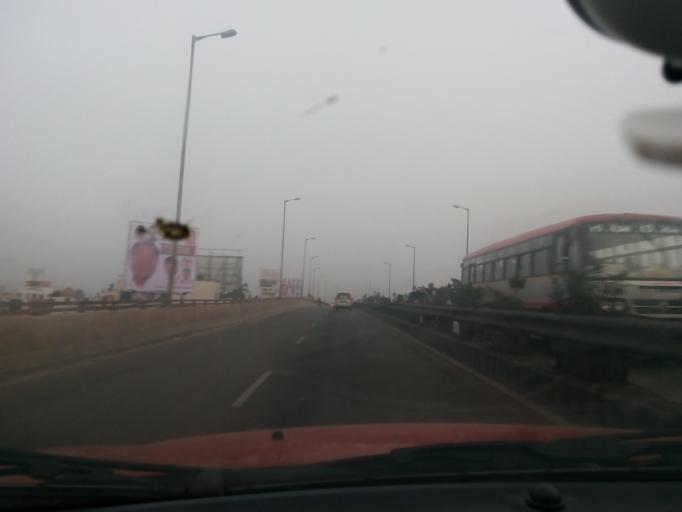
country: IN
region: Karnataka
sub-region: Bangalore Urban
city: Bangalore
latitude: 13.0349
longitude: 77.5288
